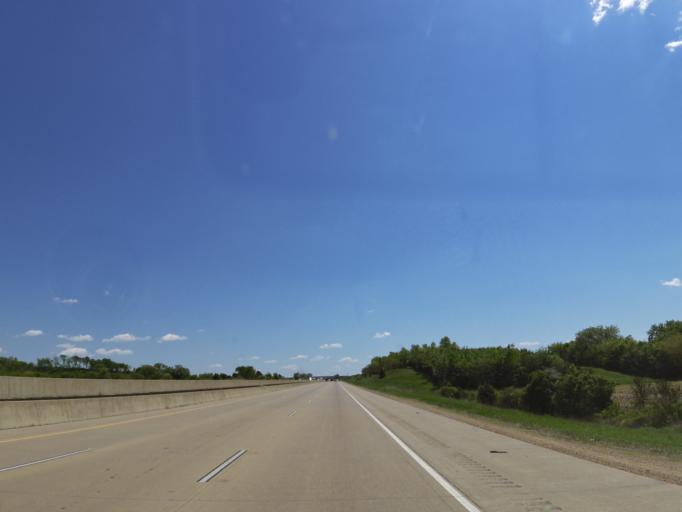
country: US
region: Wisconsin
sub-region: Columbia County
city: Poynette
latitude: 43.3607
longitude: -89.4599
